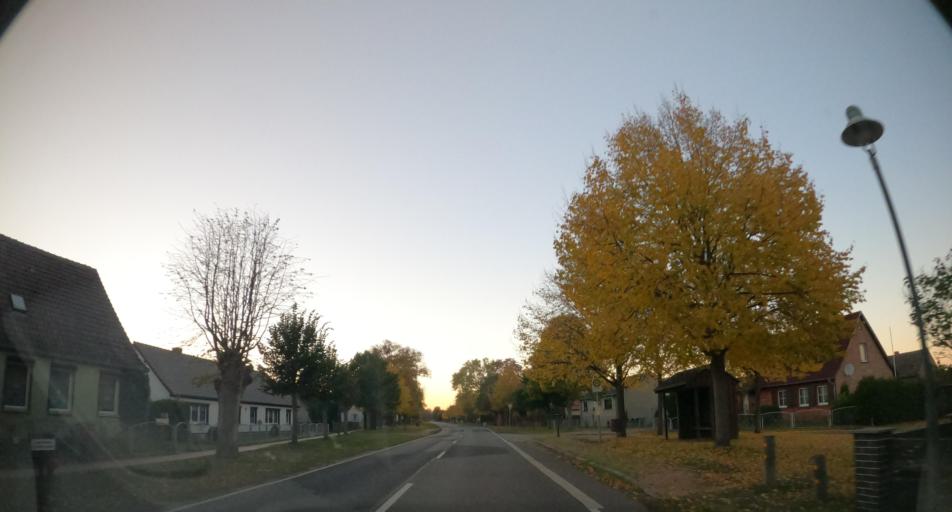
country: DE
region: Mecklenburg-Vorpommern
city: Usedom
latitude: 53.7723
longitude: 13.9063
